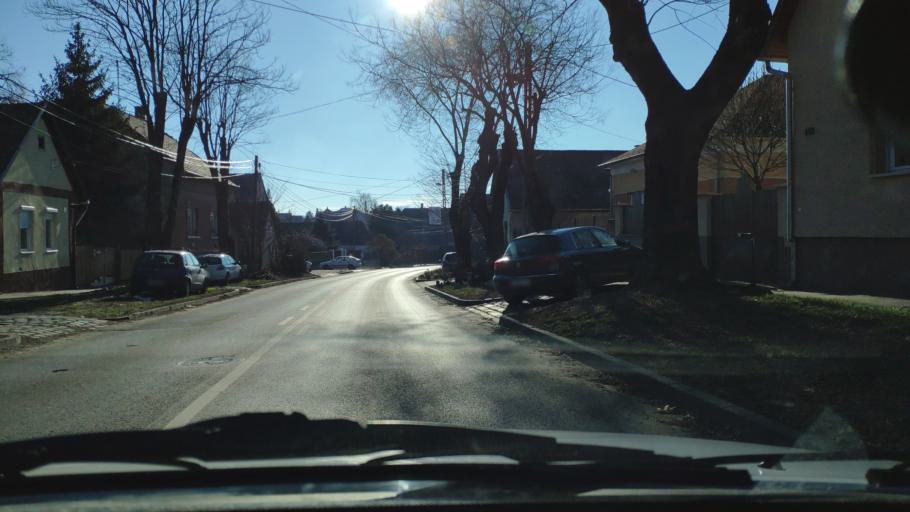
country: HU
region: Budapest
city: Budapest XXIII. keruelet
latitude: 47.3969
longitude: 19.1176
